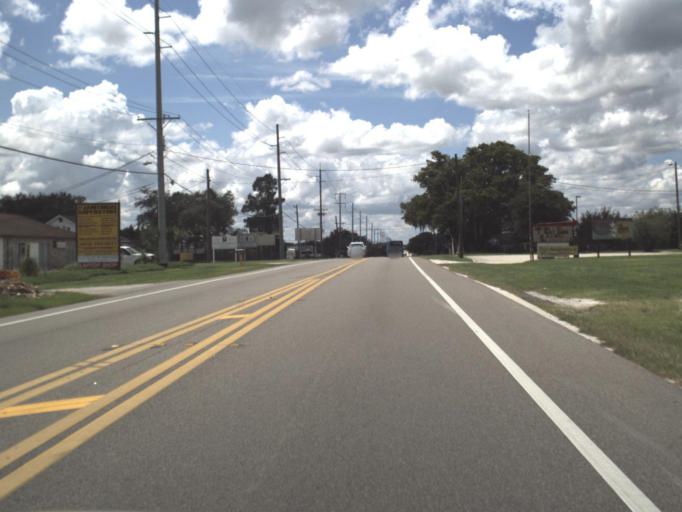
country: US
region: Florida
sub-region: Polk County
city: Cypress Gardens
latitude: 28.0225
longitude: -81.6796
